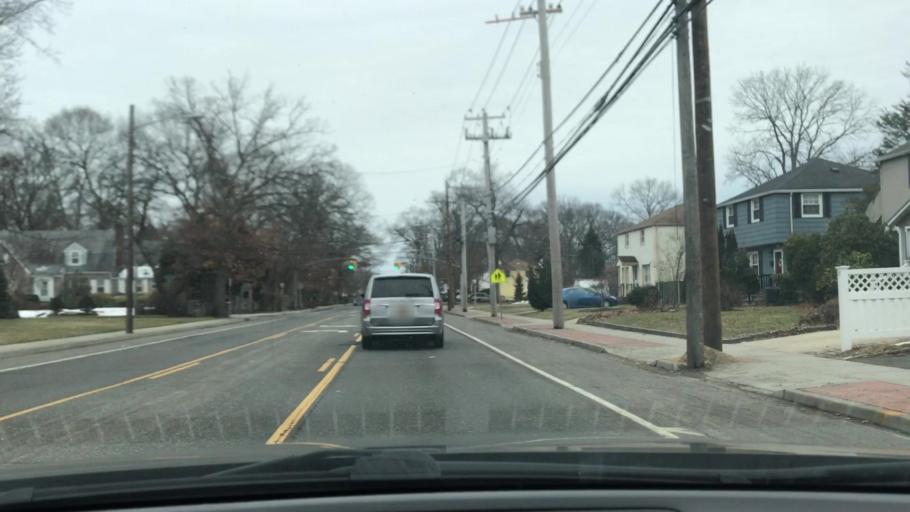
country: US
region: New York
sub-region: Nassau County
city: Merrick
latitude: 40.6721
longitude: -73.5557
